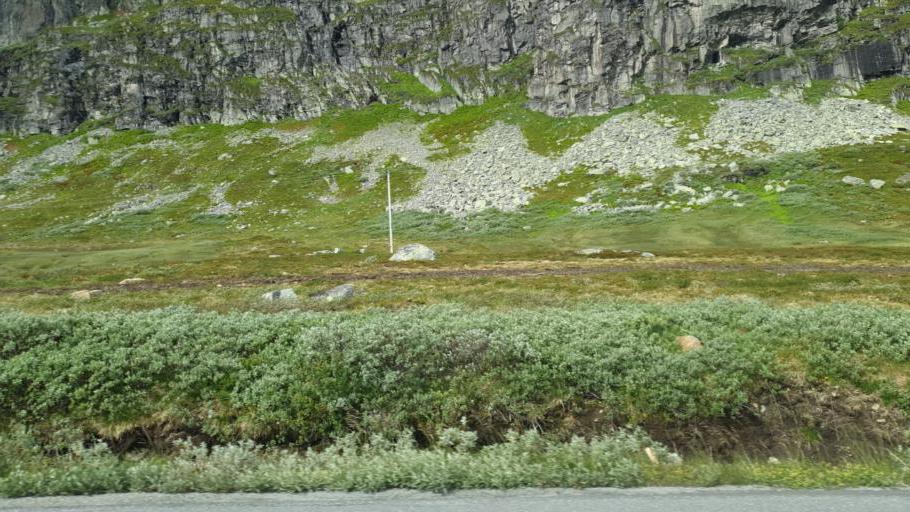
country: NO
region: Oppland
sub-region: Vestre Slidre
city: Slidre
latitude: 61.3040
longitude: 8.8078
